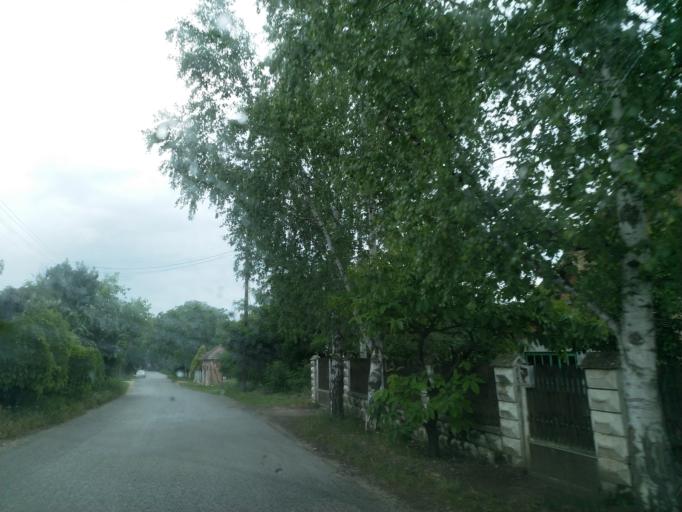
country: RS
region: Central Serbia
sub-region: Borski Okrug
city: Bor
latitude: 44.0070
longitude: 21.9845
